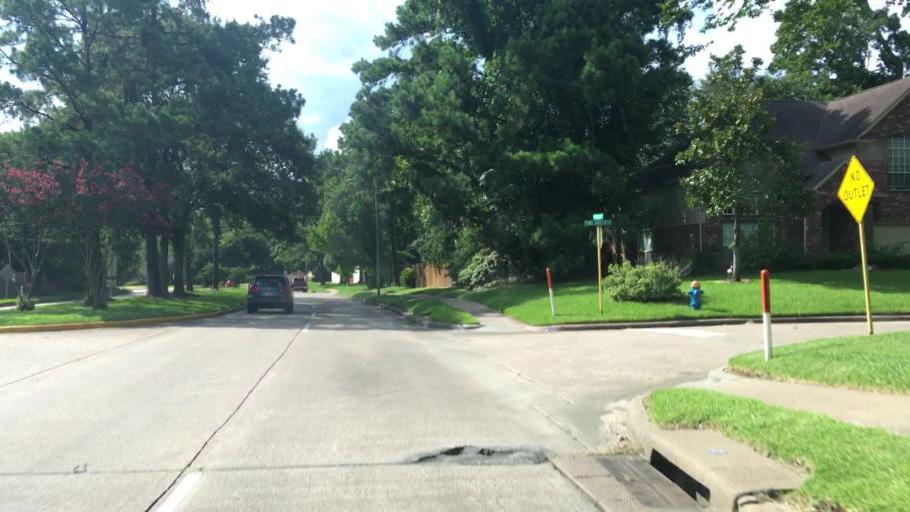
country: US
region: Texas
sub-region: Harris County
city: Atascocita
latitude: 30.0053
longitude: -95.1651
